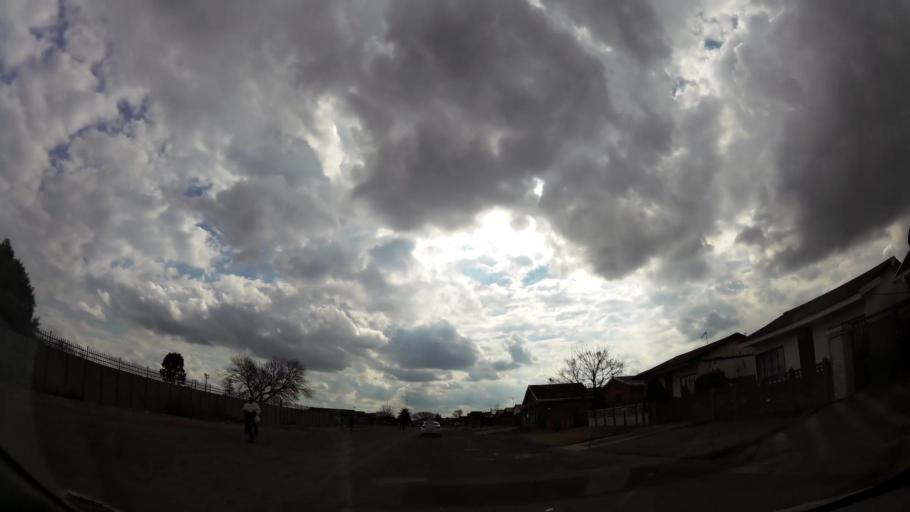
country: ZA
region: Orange Free State
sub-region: Fezile Dabi District Municipality
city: Sasolburg
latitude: -26.8477
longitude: 27.8500
